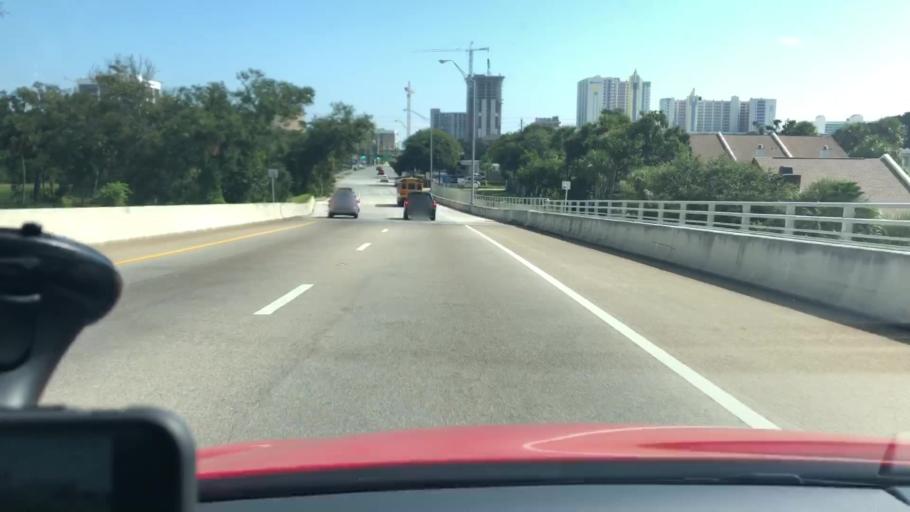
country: US
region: Florida
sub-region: Volusia County
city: Daytona Beach
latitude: 29.2311
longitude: -81.0188
